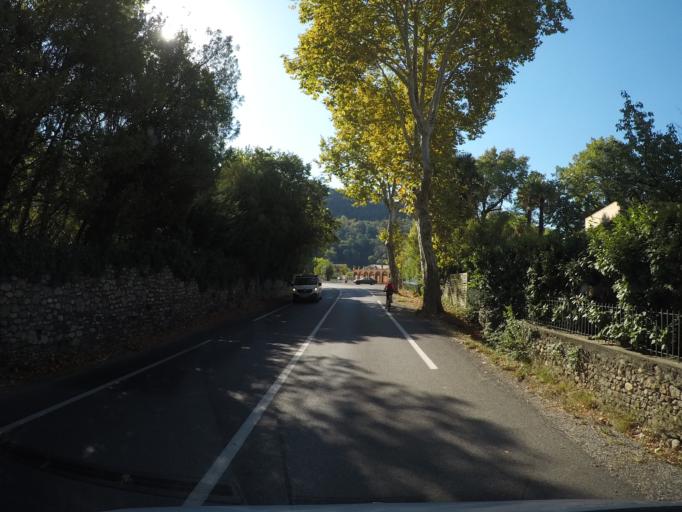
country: FR
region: Languedoc-Roussillon
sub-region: Departement du Gard
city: Anduze
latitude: 44.0596
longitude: 3.9739
